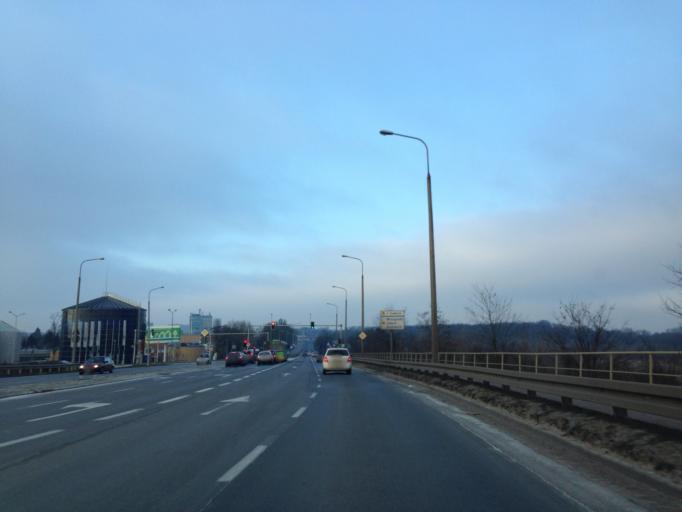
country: PL
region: Greater Poland Voivodeship
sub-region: Powiat poznanski
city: Czerwonak
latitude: 52.4300
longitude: 16.9625
